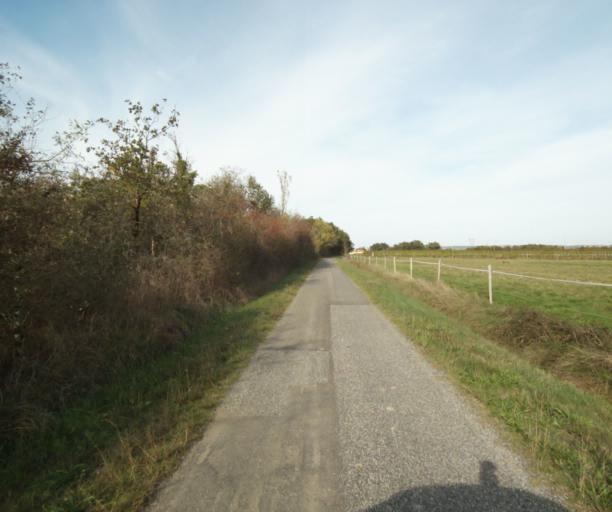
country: FR
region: Midi-Pyrenees
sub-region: Departement du Tarn-et-Garonne
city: Campsas
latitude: 43.9223
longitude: 1.3249
